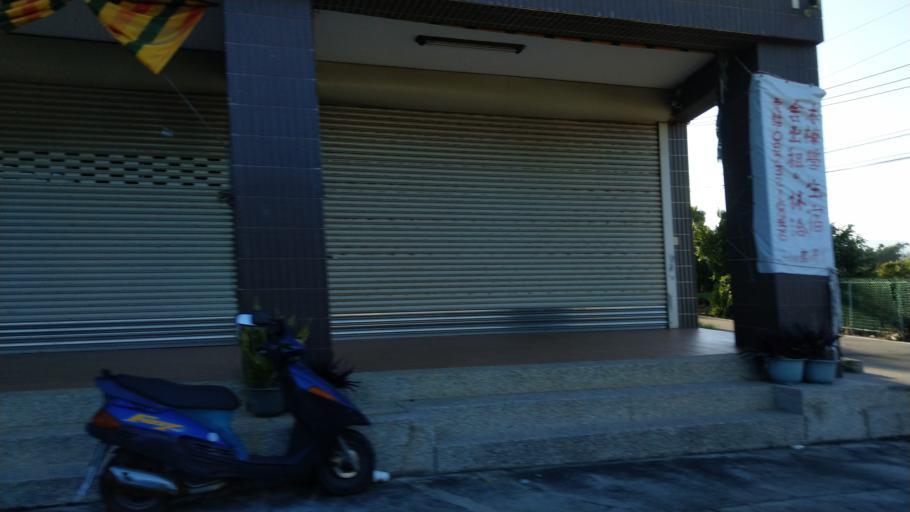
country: TW
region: Taiwan
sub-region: Miaoli
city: Miaoli
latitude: 24.5347
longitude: 120.7909
